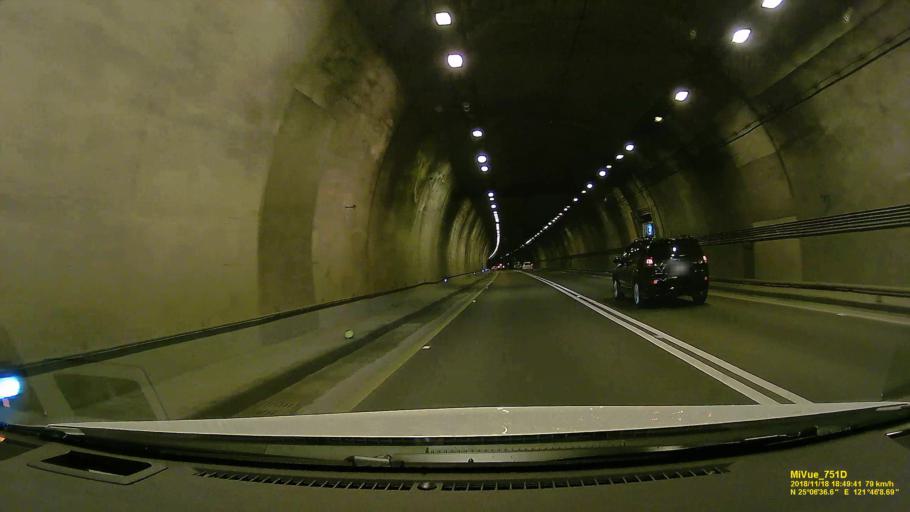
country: TW
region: Taiwan
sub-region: Keelung
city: Keelung
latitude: 25.1100
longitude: 121.7685
